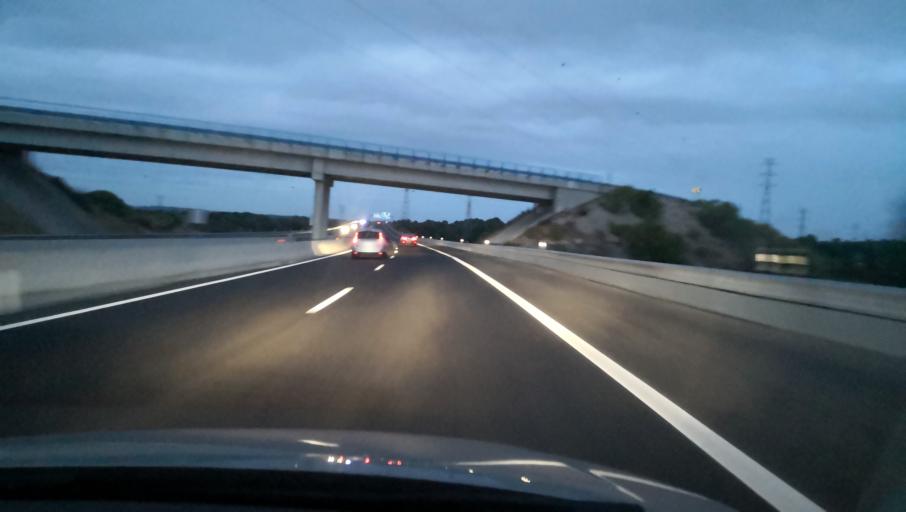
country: PT
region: Setubal
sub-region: Seixal
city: Aldeia de Paio Pires
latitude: 38.5850
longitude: -9.0689
